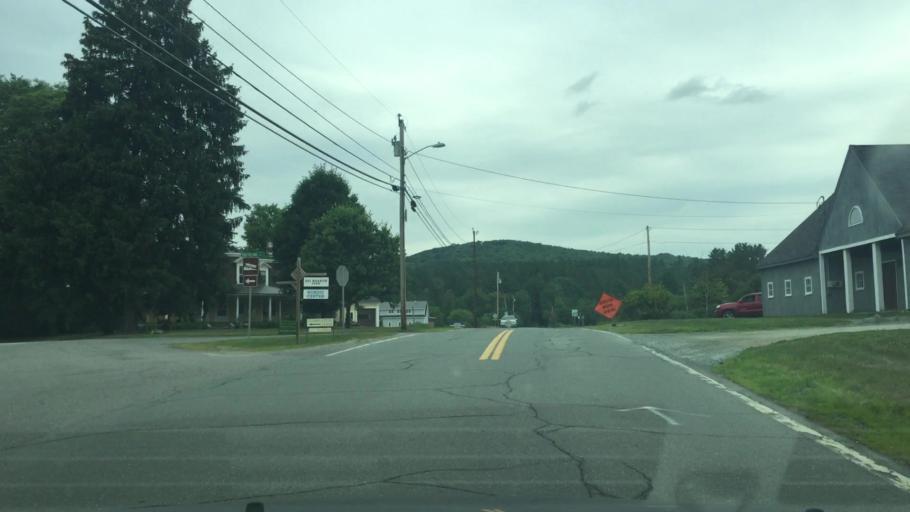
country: US
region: New Hampshire
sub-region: Grafton County
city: Littleton
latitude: 44.2427
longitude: -71.7614
